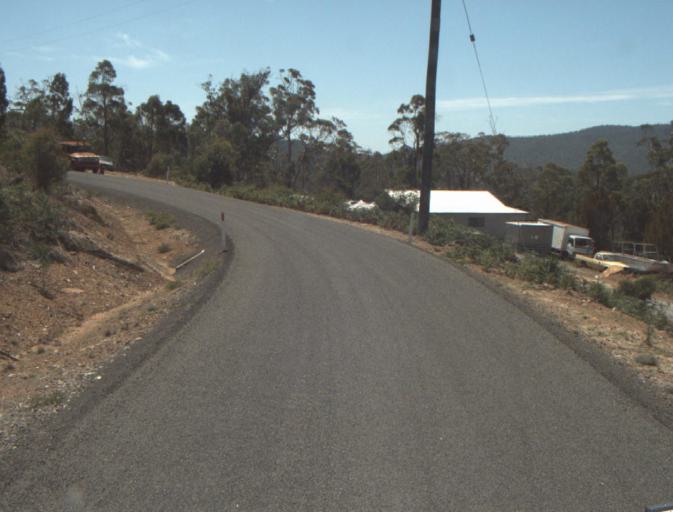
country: AU
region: Tasmania
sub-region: Launceston
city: Mayfield
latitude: -41.3199
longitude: 147.1227
